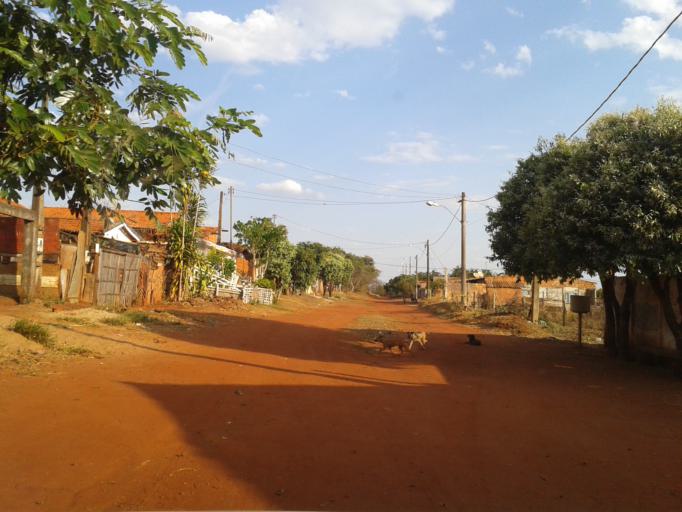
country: BR
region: Minas Gerais
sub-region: Ituiutaba
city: Ituiutaba
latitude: -18.9940
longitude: -49.4356
